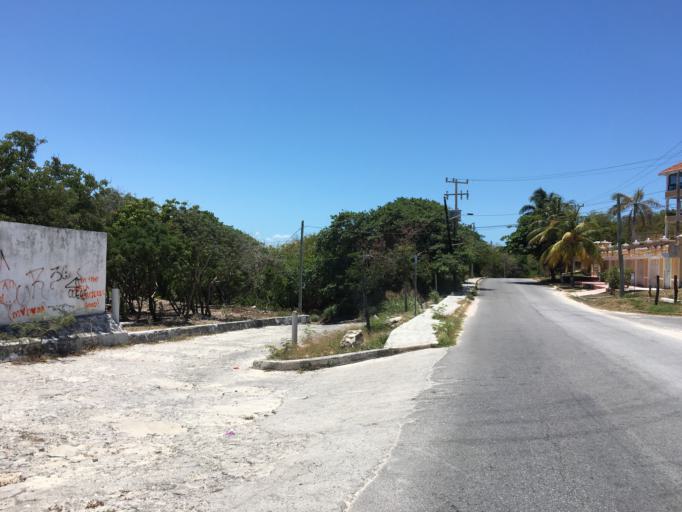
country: MX
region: Quintana Roo
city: Isla Mujeres
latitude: 21.2139
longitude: -86.7234
